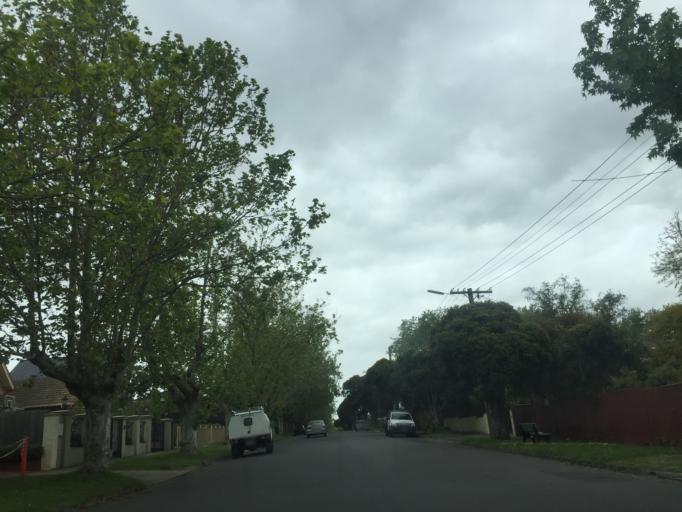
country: AU
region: Victoria
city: Balwyn
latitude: -37.8101
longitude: 145.0560
